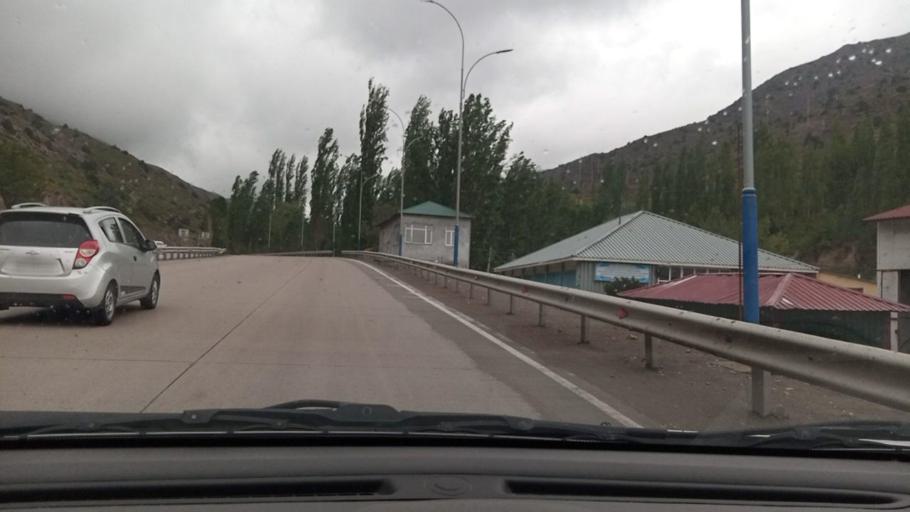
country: TJ
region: Viloyati Sughd
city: Shaydon
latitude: 41.0397
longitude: 70.5786
